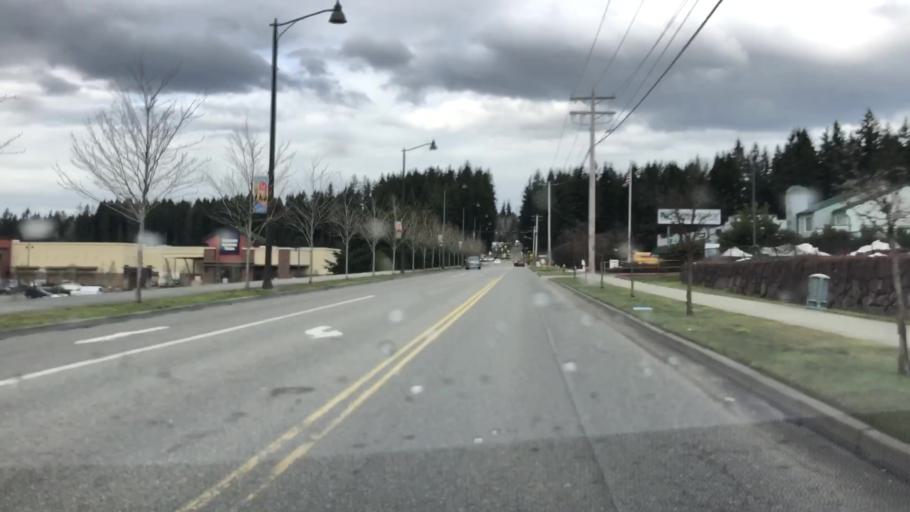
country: US
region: Washington
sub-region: Snohomish County
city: Monroe
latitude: 47.8611
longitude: -121.9695
